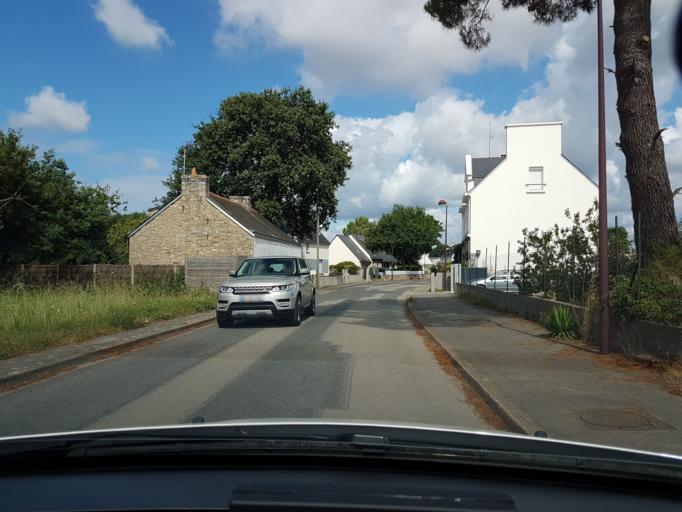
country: FR
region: Brittany
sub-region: Departement du Morbihan
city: Sainte-Helene
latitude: 47.7185
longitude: -3.2011
